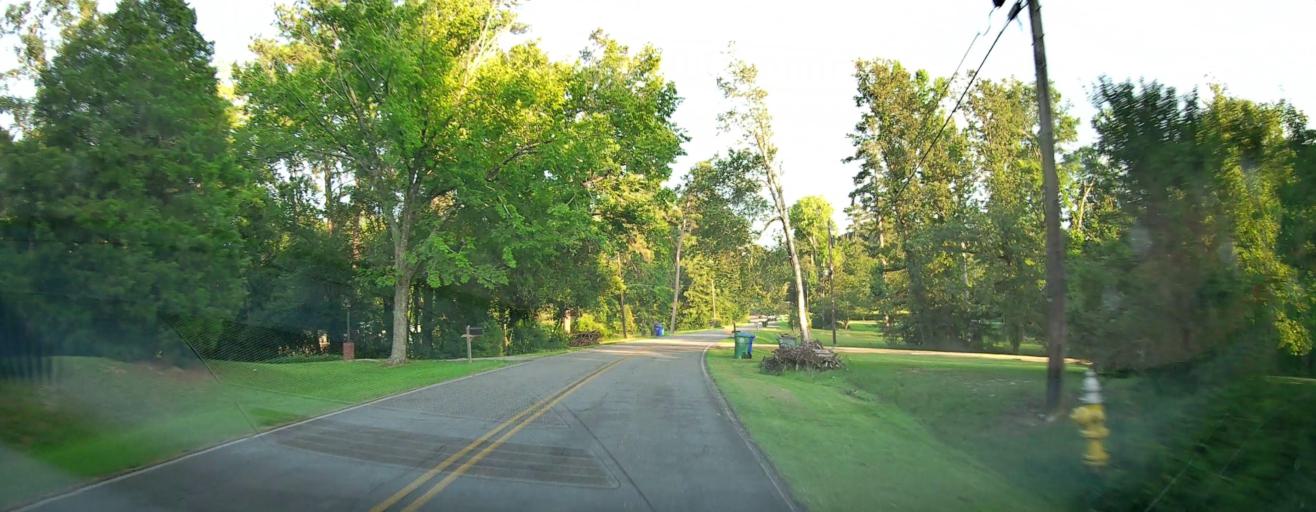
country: US
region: Georgia
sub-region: Bibb County
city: Macon
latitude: 32.8782
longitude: -83.6897
